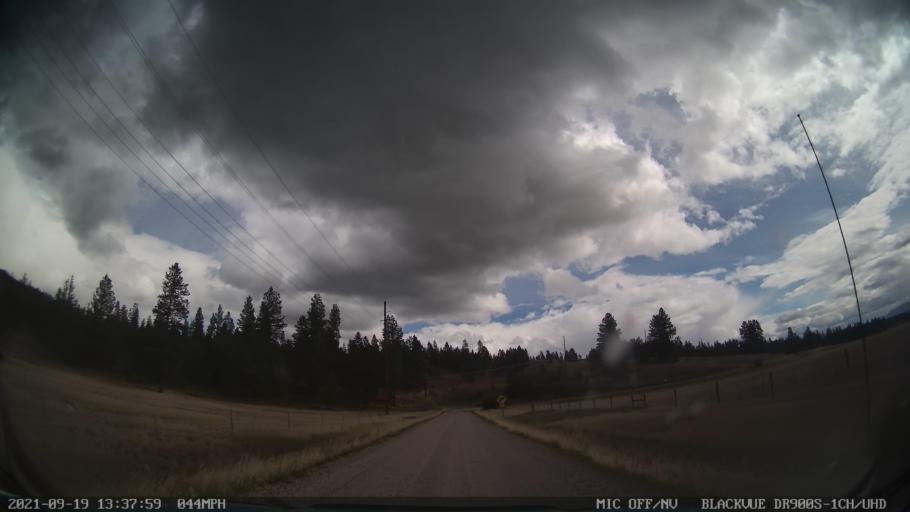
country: US
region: Montana
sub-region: Missoula County
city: Seeley Lake
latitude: 47.1066
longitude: -113.2745
